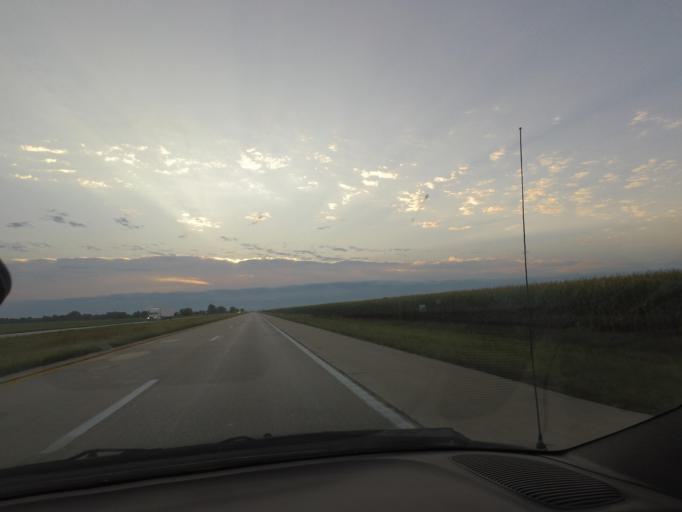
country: US
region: Missouri
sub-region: Macon County
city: Macon
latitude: 39.7501
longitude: -92.3449
